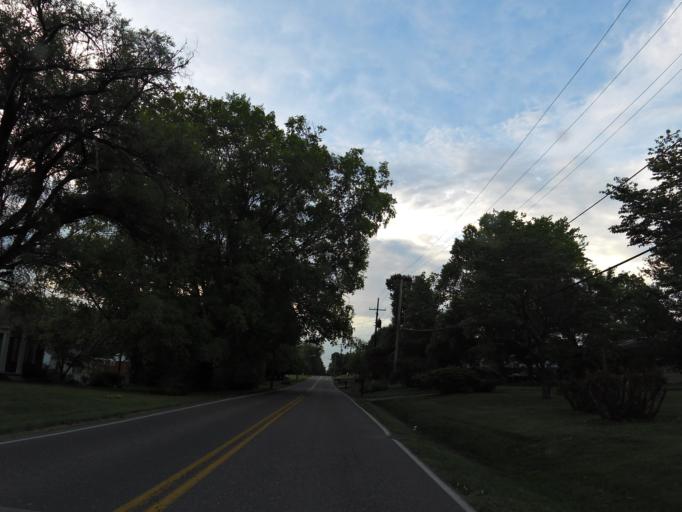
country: US
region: Tennessee
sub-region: Knox County
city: Knoxville
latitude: 36.0359
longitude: -83.9055
